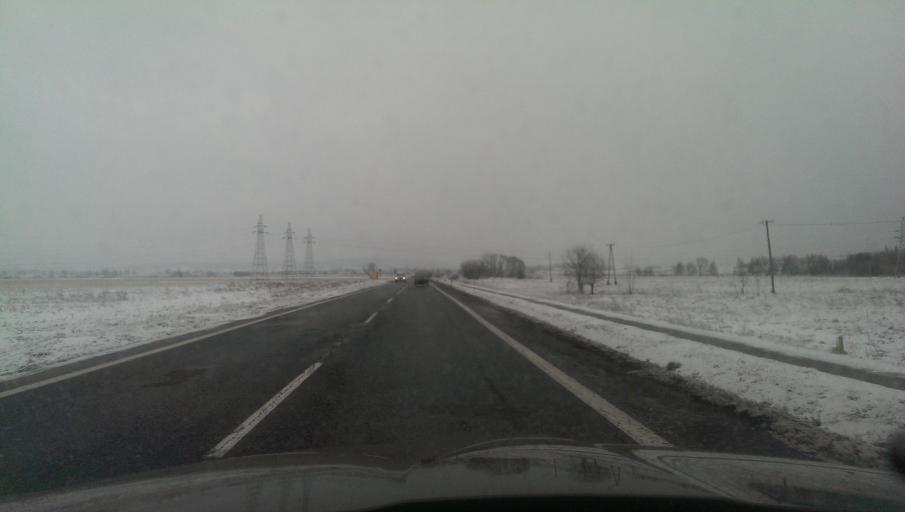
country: PL
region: Subcarpathian Voivodeship
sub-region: Powiat sanocki
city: Besko
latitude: 49.5843
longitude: 21.9760
